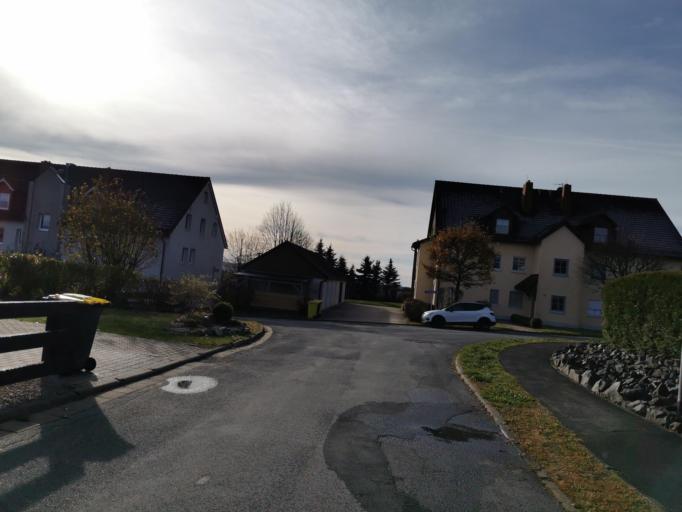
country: DE
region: Bavaria
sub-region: Upper Franconia
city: Teuschnitz
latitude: 50.4388
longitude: 11.3749
